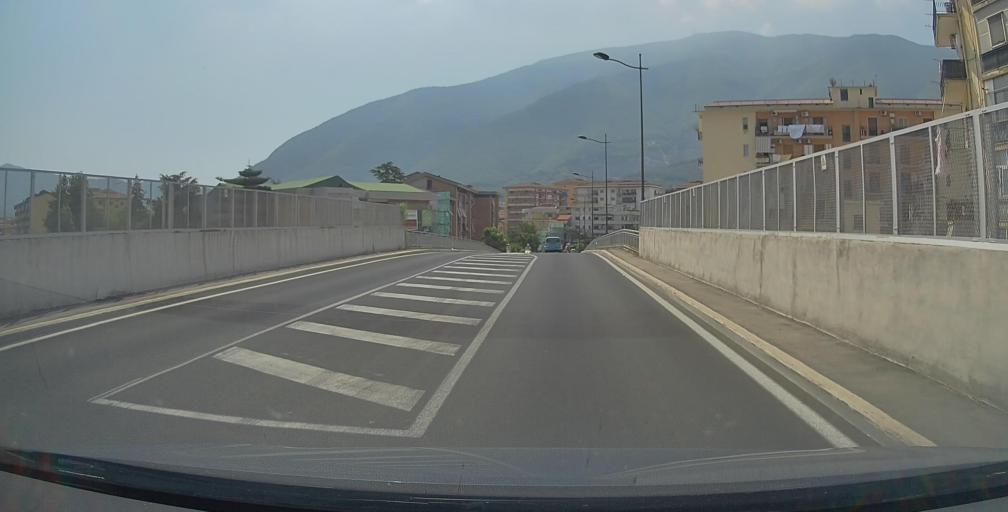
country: IT
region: Campania
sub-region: Provincia di Salerno
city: Nocera Inferiore
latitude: 40.7433
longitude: 14.6487
